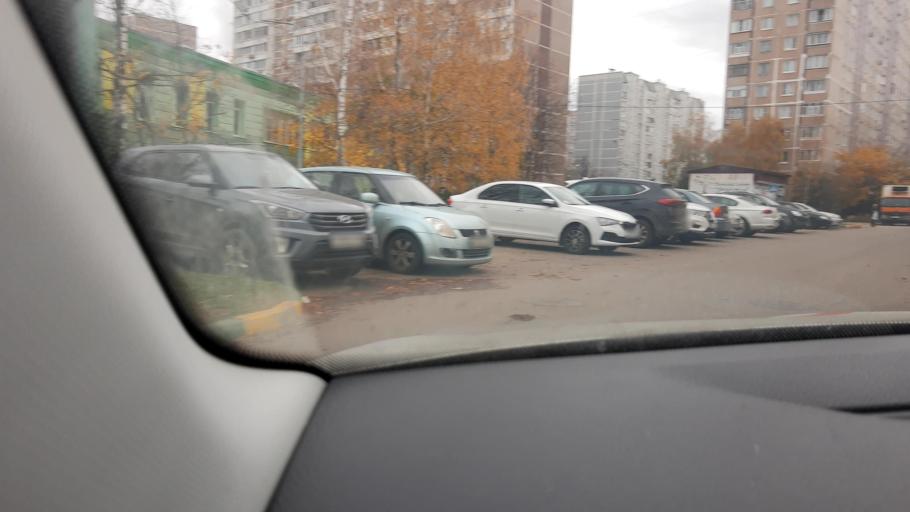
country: RU
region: Moskovskaya
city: Vidnoye
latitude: 55.5453
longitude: 37.7133
